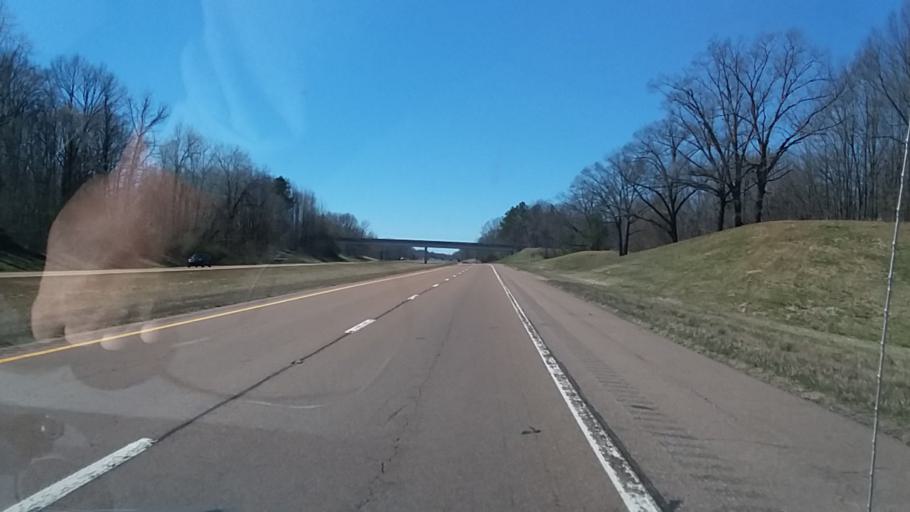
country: US
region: Tennessee
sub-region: Dyer County
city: Dyersburg
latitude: 36.0695
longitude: -89.4228
